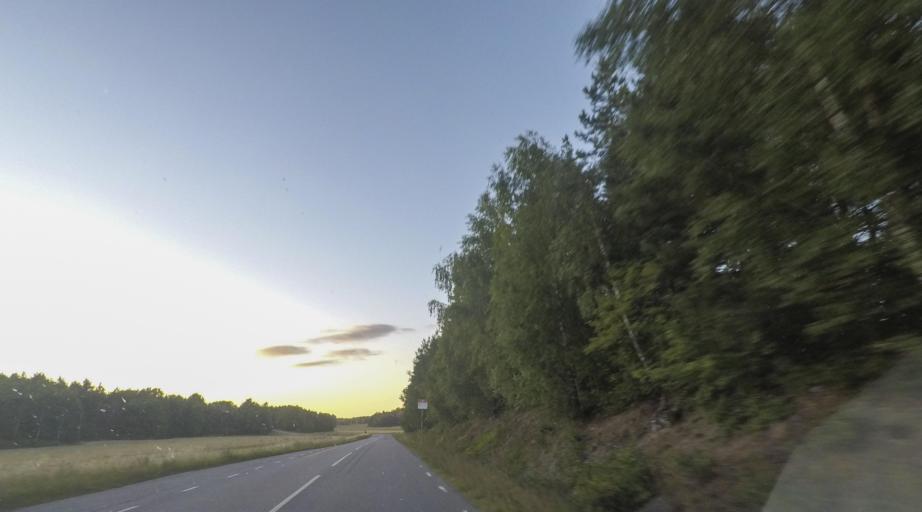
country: SE
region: Soedermanland
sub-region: Trosa Kommun
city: Trosa
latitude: 58.9763
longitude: 17.6929
